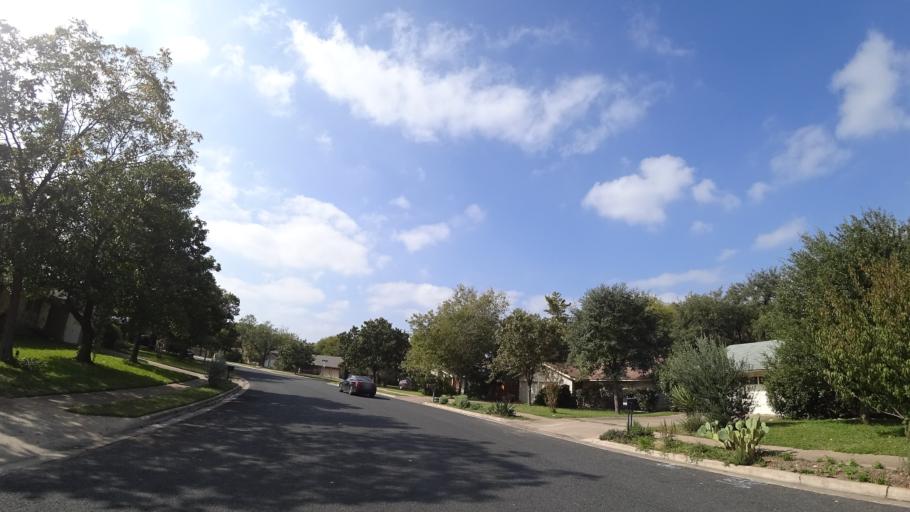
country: US
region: Texas
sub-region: Travis County
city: Shady Hollow
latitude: 30.2042
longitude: -97.8119
